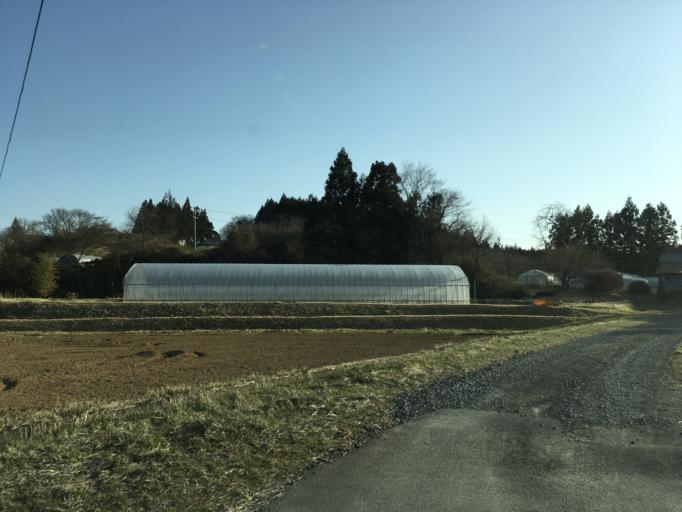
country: JP
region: Iwate
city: Ichinoseki
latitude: 38.8368
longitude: 141.1365
